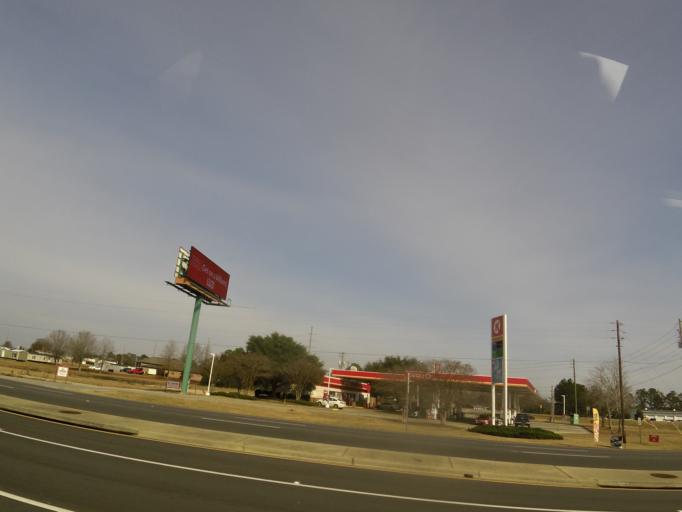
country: US
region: Alabama
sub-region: Dale County
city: Midland City
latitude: 31.2709
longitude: -85.4485
